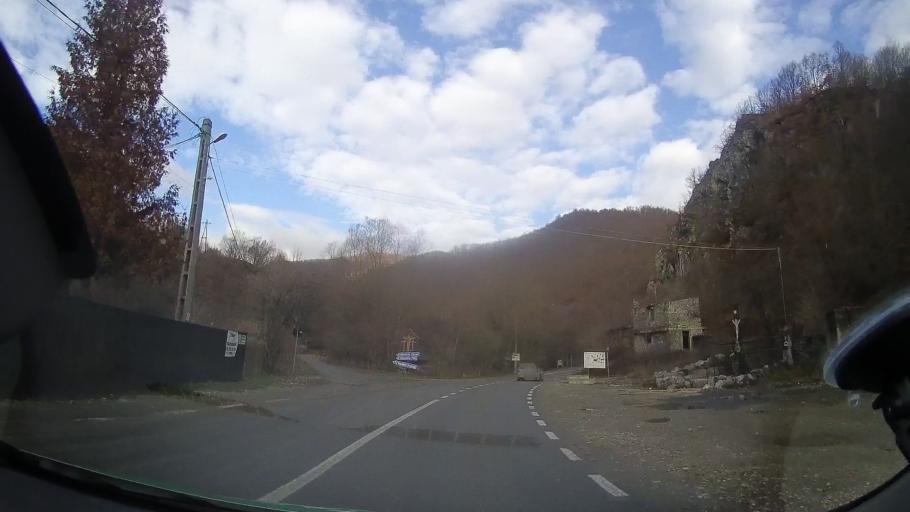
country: RO
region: Cluj
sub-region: Comuna Baisoara
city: Baisoara
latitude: 46.6059
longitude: 23.4188
